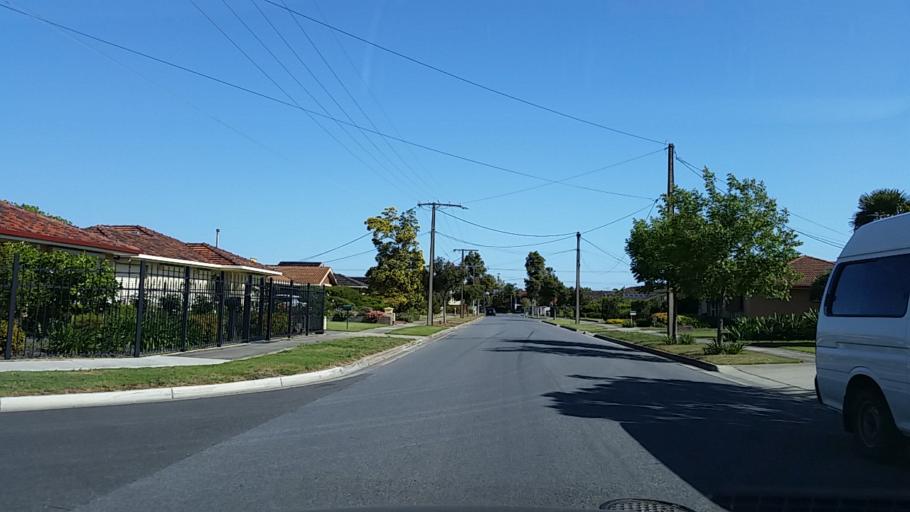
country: AU
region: South Australia
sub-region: Charles Sturt
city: Seaton
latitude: -34.9110
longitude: 138.5092
